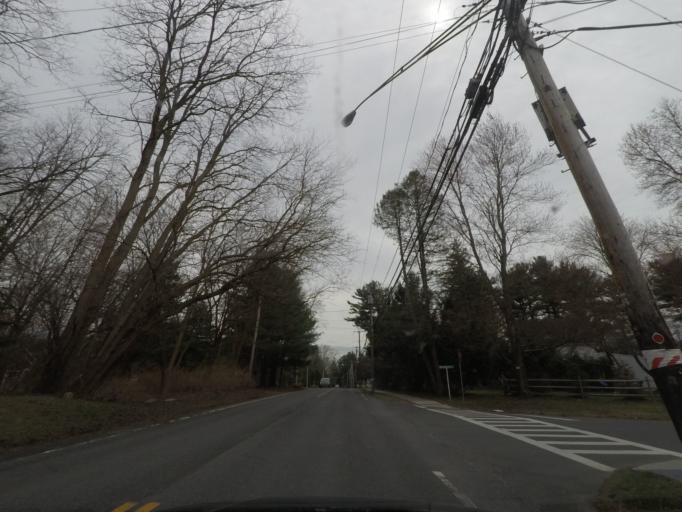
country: US
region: New York
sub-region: Albany County
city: Delmar
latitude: 42.6143
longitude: -73.8205
